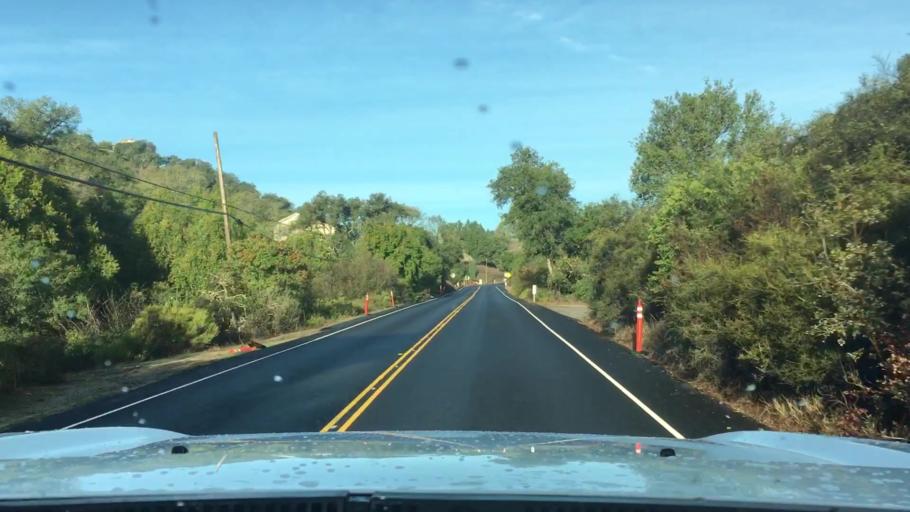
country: US
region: California
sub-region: San Luis Obispo County
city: Atascadero
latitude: 35.4535
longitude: -120.7116
